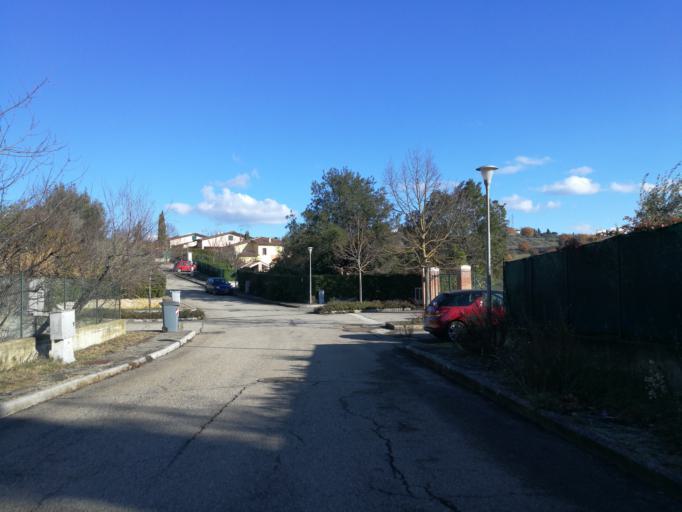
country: IT
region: Umbria
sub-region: Provincia di Perugia
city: Perugia
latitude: 43.0785
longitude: 12.3817
